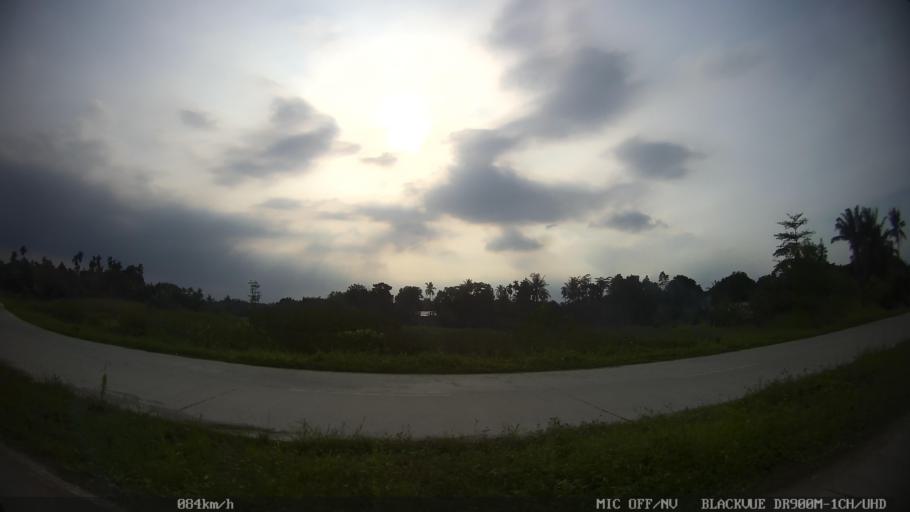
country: ID
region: North Sumatra
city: Binjai
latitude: 3.6015
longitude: 98.5335
